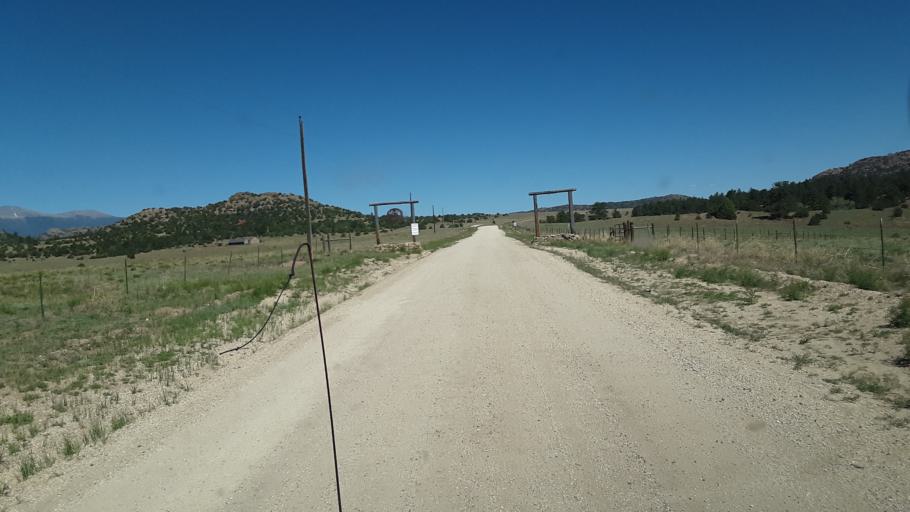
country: US
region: Colorado
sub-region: Custer County
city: Westcliffe
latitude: 38.2166
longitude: -105.4494
